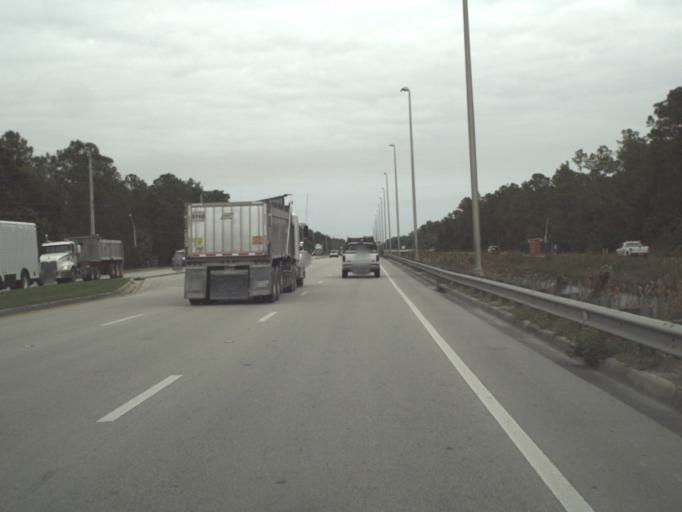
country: US
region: Florida
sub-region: Collier County
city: Lely Resort
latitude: 26.1208
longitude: -81.6869
